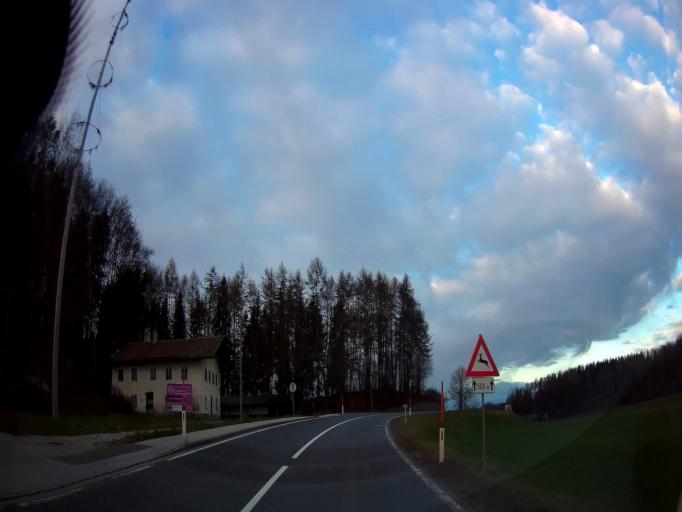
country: AT
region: Salzburg
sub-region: Politischer Bezirk Salzburg-Umgebung
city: Dorfbeuern
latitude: 48.0823
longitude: 12.9916
